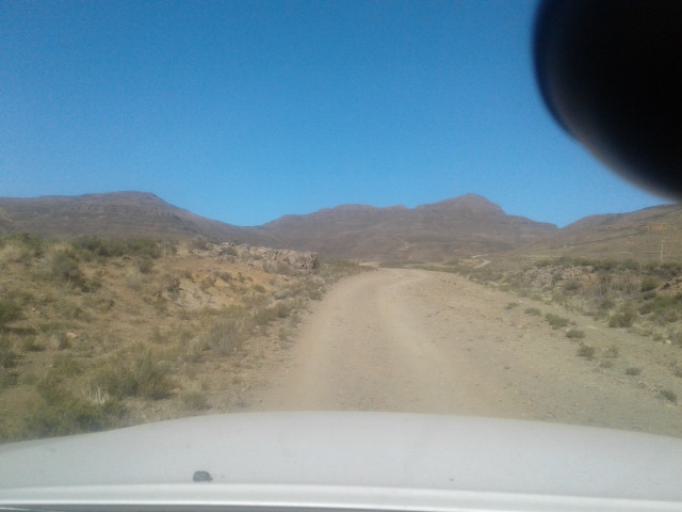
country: LS
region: Maseru
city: Nako
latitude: -29.3925
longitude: 28.0039
